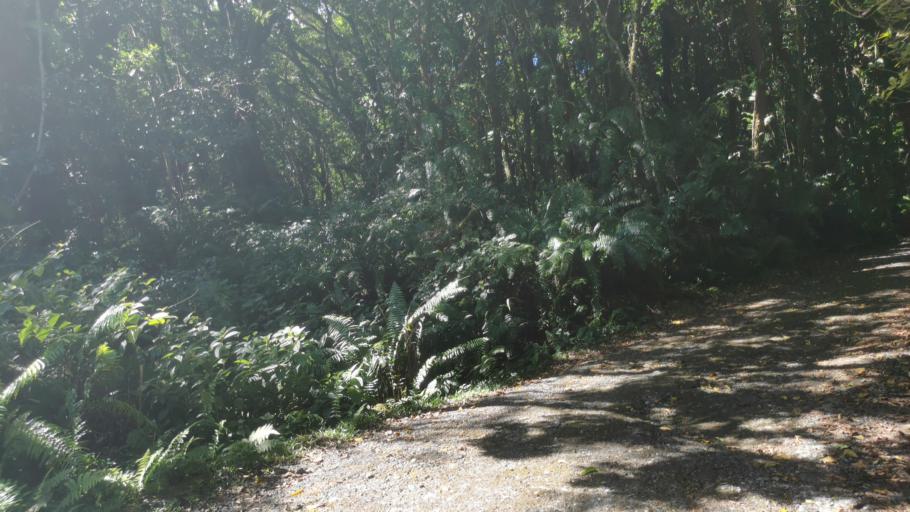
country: RE
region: Reunion
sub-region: Reunion
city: Saint-Philippe
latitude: -21.3561
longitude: 55.7390
